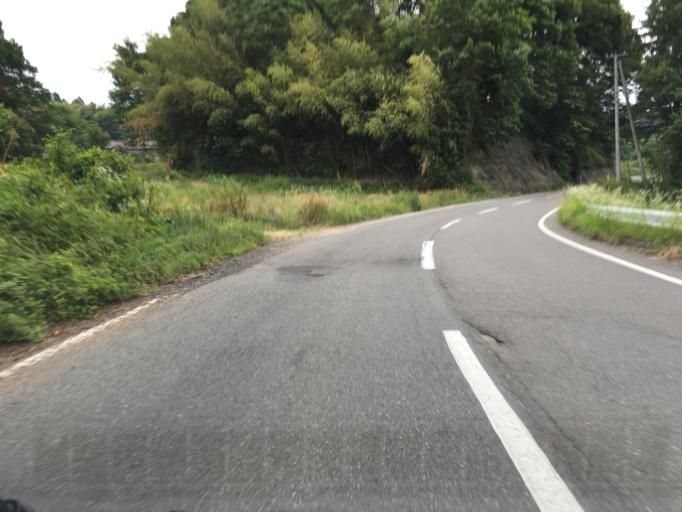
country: JP
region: Fukushima
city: Nihommatsu
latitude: 37.6209
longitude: 140.5395
